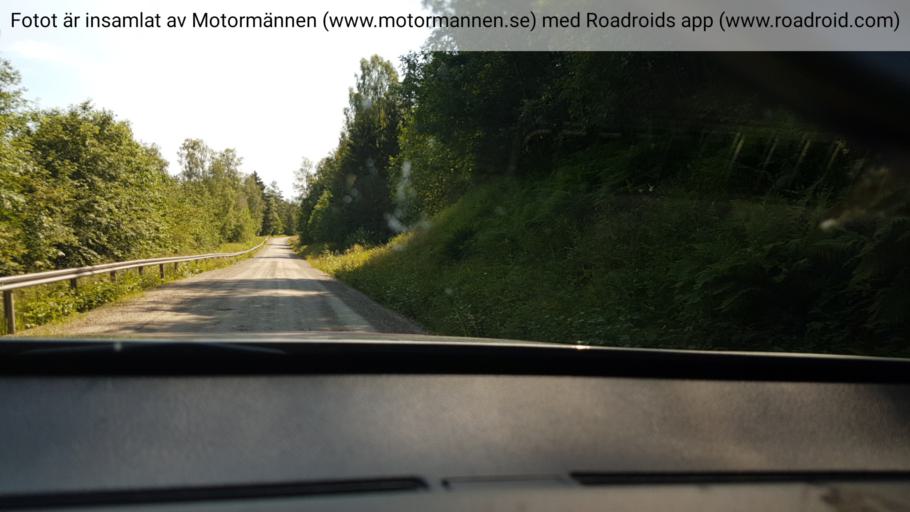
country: SE
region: Vaermland
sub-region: Torsby Kommun
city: Torsby
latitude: 60.4463
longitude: 13.2145
